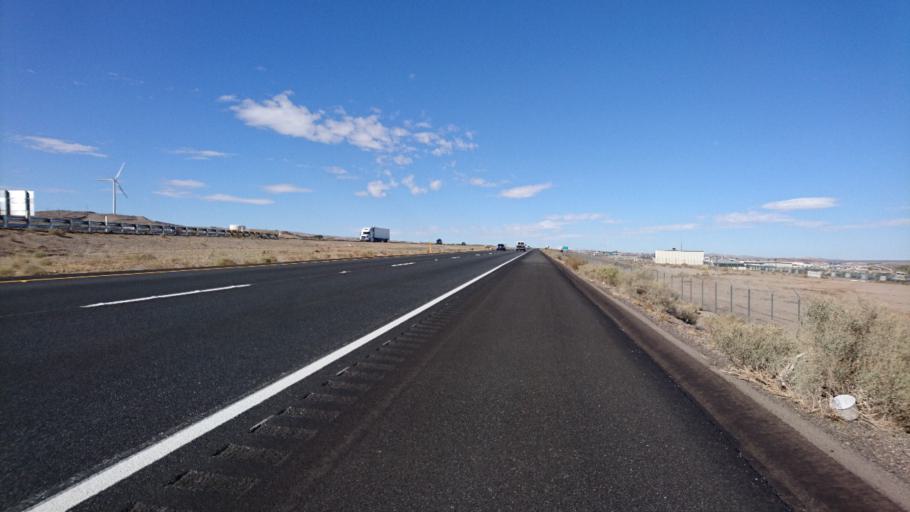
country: US
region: California
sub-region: San Bernardino County
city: Barstow
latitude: 34.8671
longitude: -116.9476
